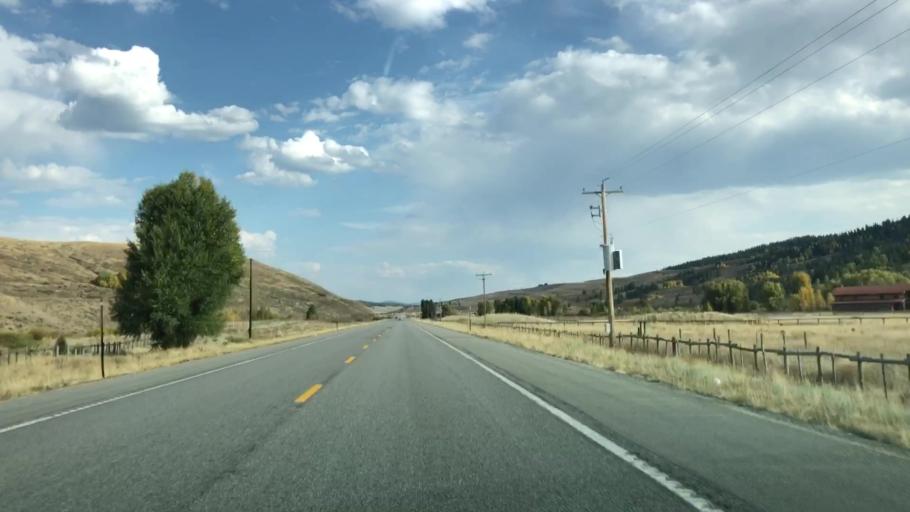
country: US
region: Wyoming
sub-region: Teton County
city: Hoback
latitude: 43.2386
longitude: -110.4468
